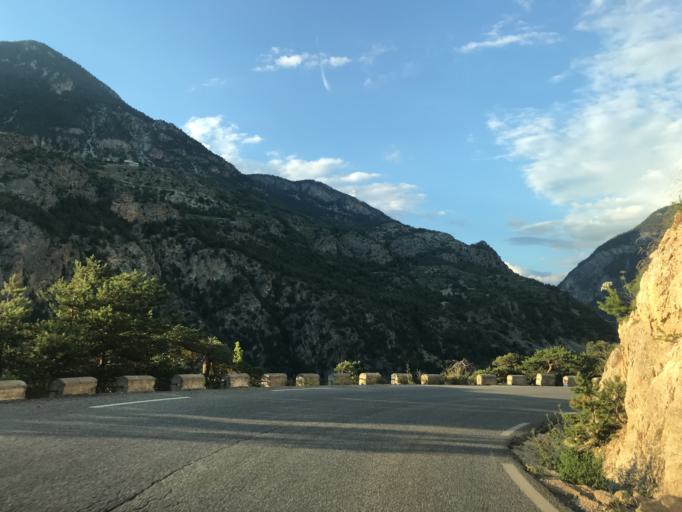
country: FR
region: Provence-Alpes-Cote d'Azur
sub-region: Departement des Hautes-Alpes
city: Guillestre
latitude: 44.6665
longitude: 6.6686
